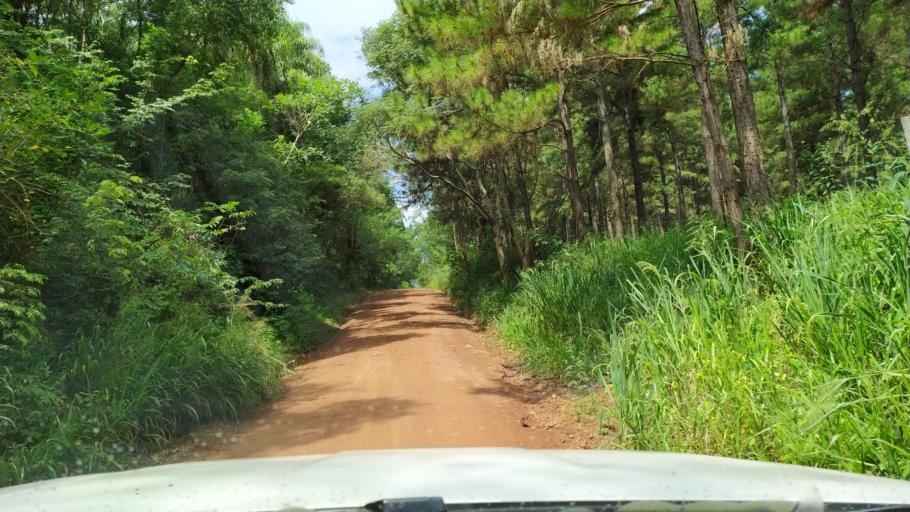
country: AR
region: Misiones
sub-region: Departamento de Eldorado
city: Eldorado
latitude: -26.4501
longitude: -54.6019
